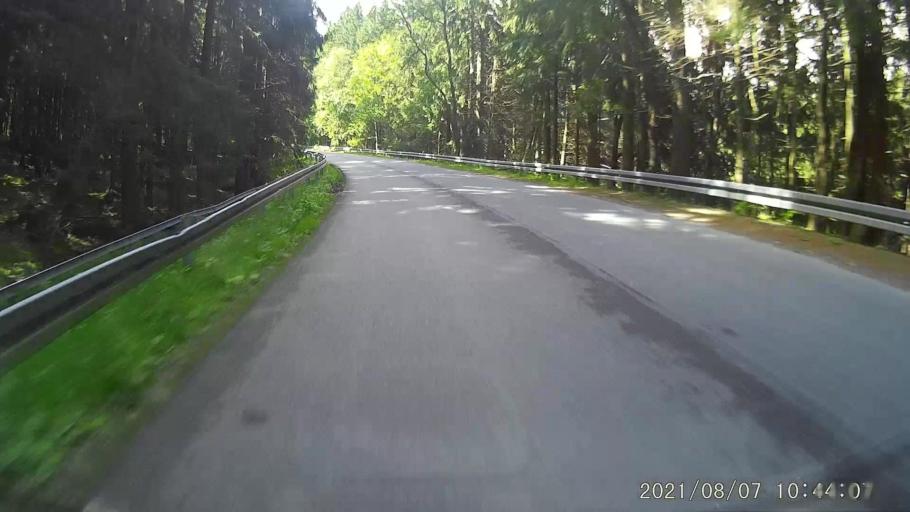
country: PL
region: Lower Silesian Voivodeship
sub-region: Powiat klodzki
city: Duszniki-Zdroj
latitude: 50.3296
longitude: 16.4035
